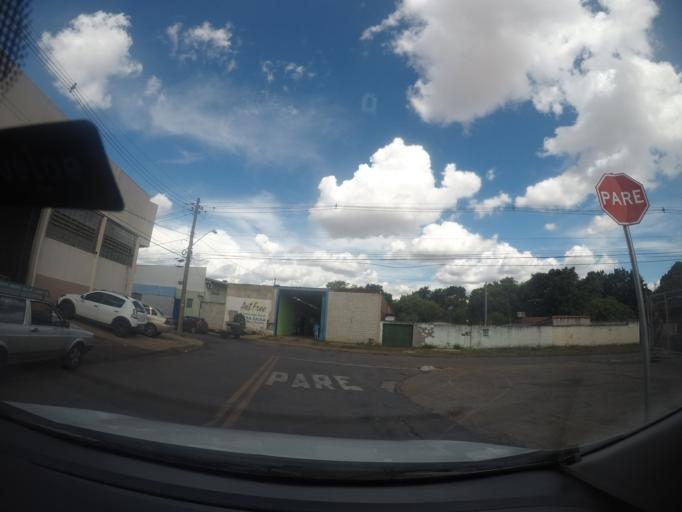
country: BR
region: Goias
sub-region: Goiania
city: Goiania
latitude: -16.6735
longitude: -49.3010
